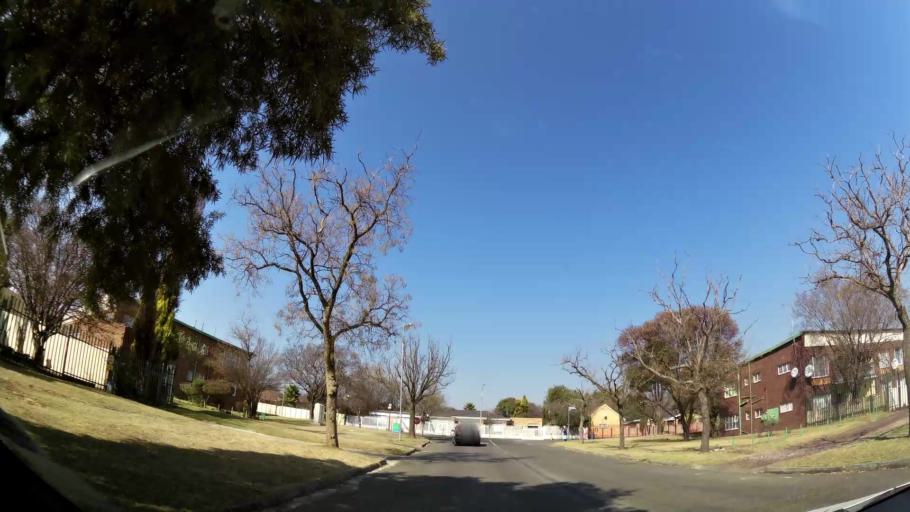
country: ZA
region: Gauteng
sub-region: Ekurhuleni Metropolitan Municipality
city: Boksburg
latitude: -26.2413
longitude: 28.2540
